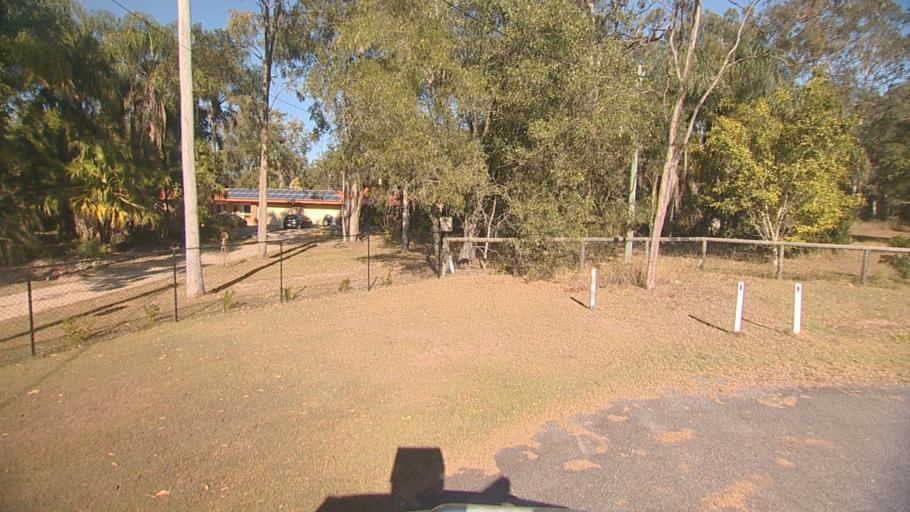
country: AU
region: Queensland
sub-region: Logan
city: Chambers Flat
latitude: -27.7514
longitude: 153.0508
